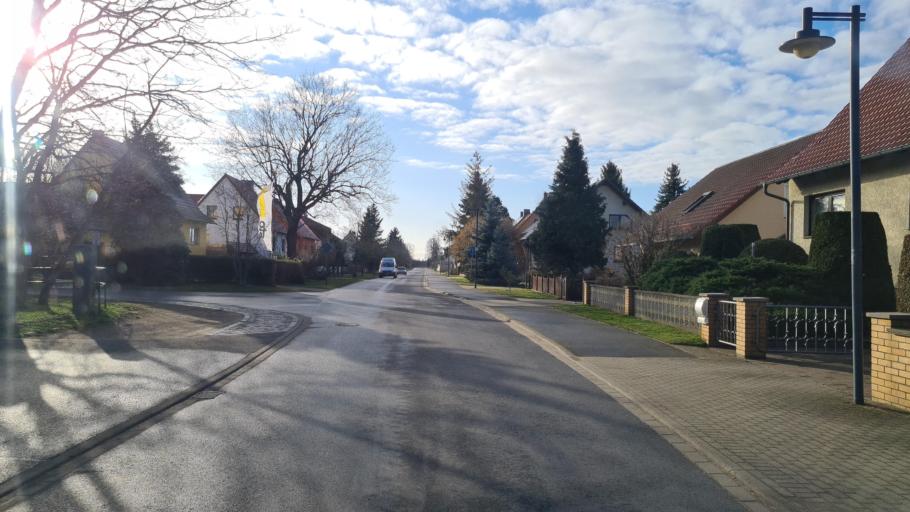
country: DE
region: Brandenburg
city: Herzberg
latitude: 51.7016
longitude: 13.2164
